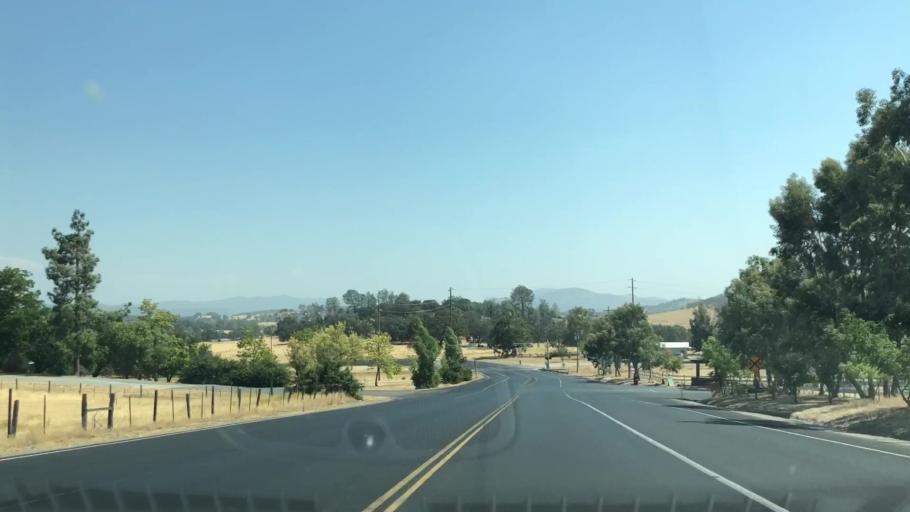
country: US
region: California
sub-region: Tuolumne County
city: Jamestown
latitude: 37.8790
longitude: -120.4622
